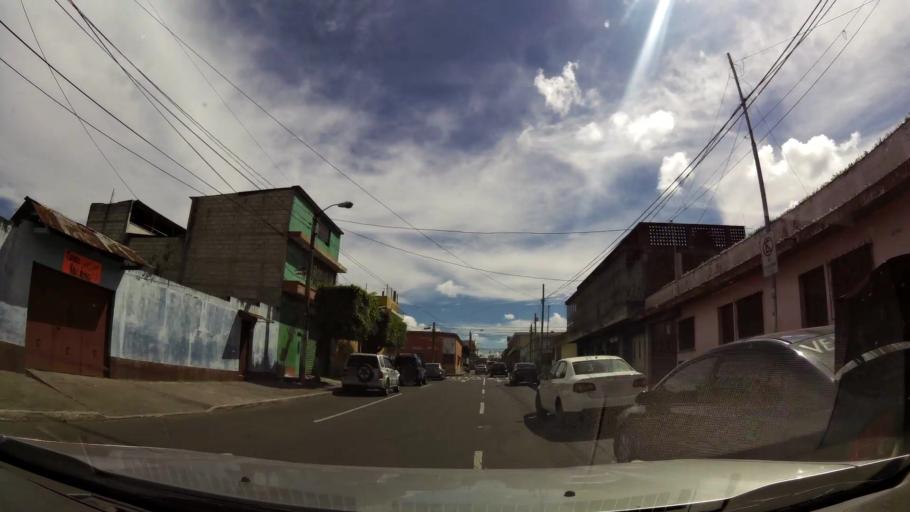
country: GT
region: Guatemala
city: Mixco
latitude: 14.6519
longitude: -90.5834
